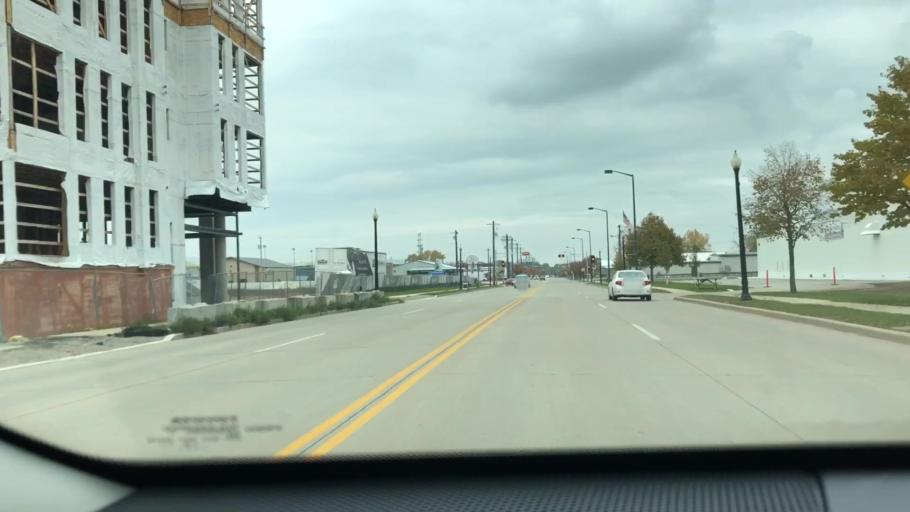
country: US
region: Wisconsin
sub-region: Brown County
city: Ashwaubenon
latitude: 44.4926
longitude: -88.0570
